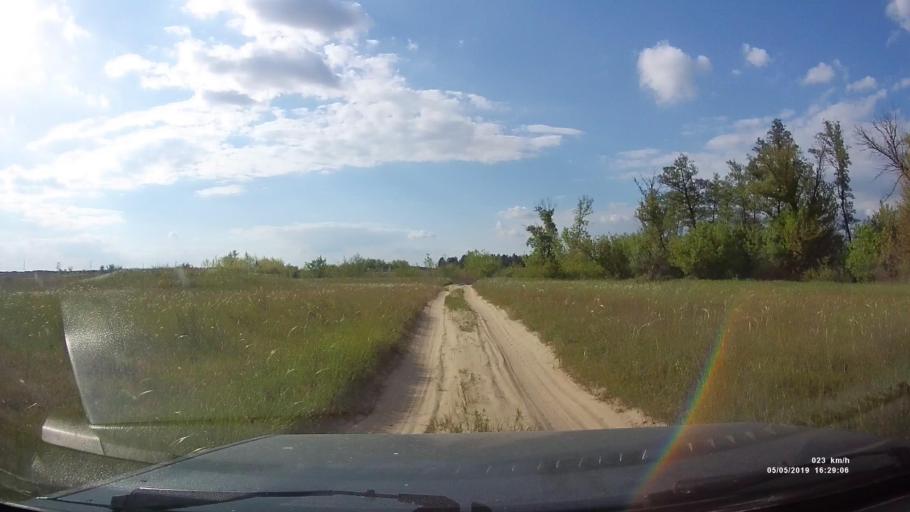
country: RU
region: Rostov
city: Ust'-Donetskiy
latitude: 47.7695
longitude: 41.0148
